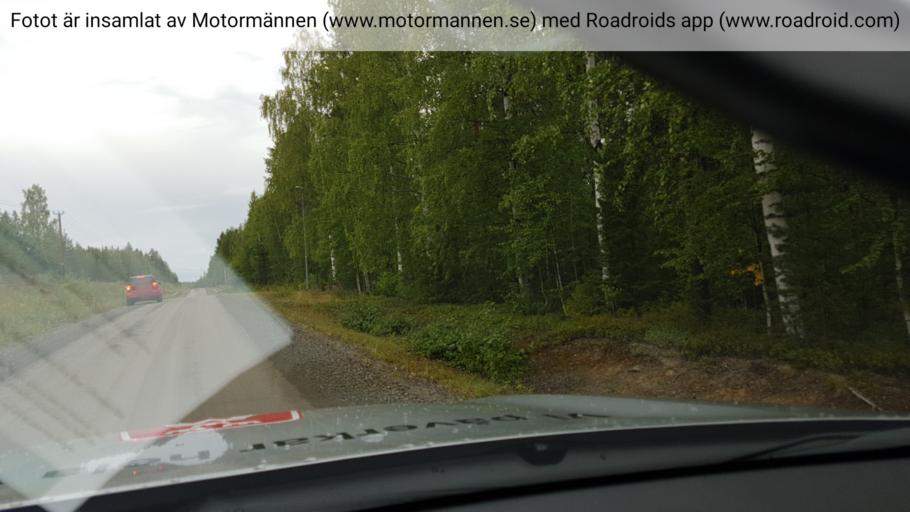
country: SE
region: Norrbotten
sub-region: Alvsbyns Kommun
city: AElvsbyn
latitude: 65.9923
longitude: 21.1905
